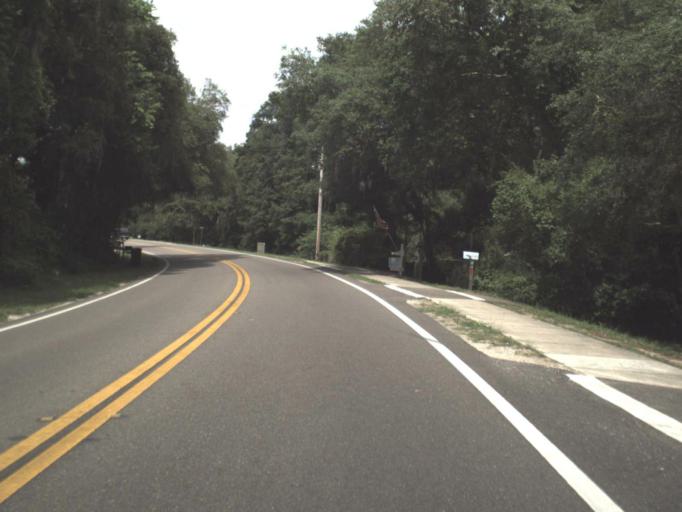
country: US
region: Florida
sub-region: Clay County
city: Keystone Heights
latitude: 29.7711
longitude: -82.0369
